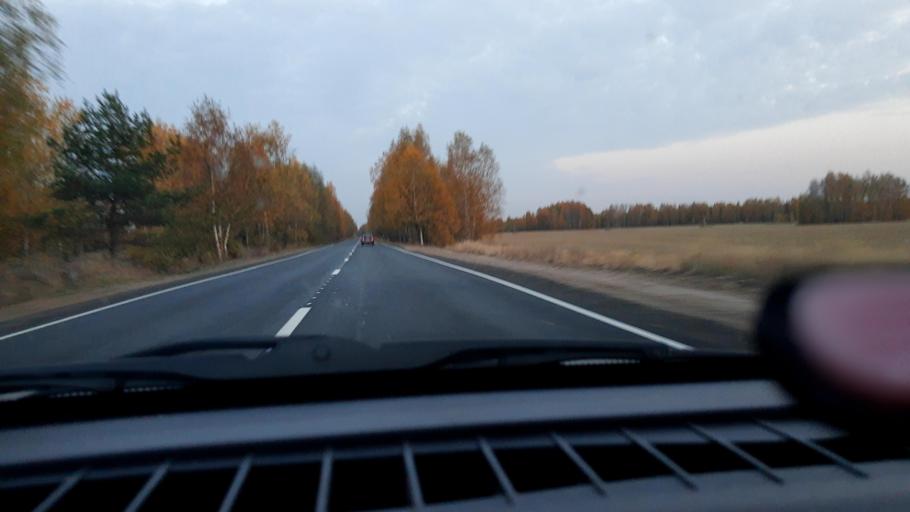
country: RU
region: Nizjnij Novgorod
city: Novaya Balakhna
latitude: 56.5579
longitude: 43.7352
